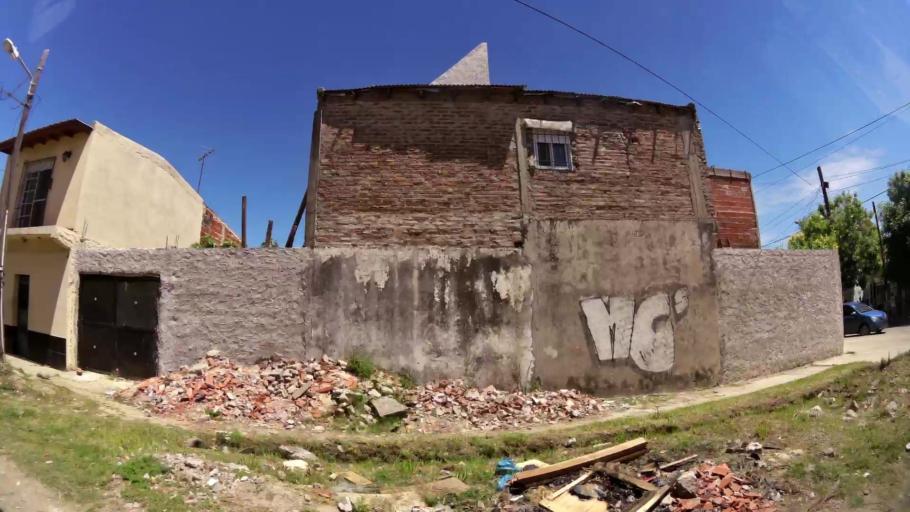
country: AR
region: Buenos Aires
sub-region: Partido de Quilmes
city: Quilmes
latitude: -34.7247
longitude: -58.3224
